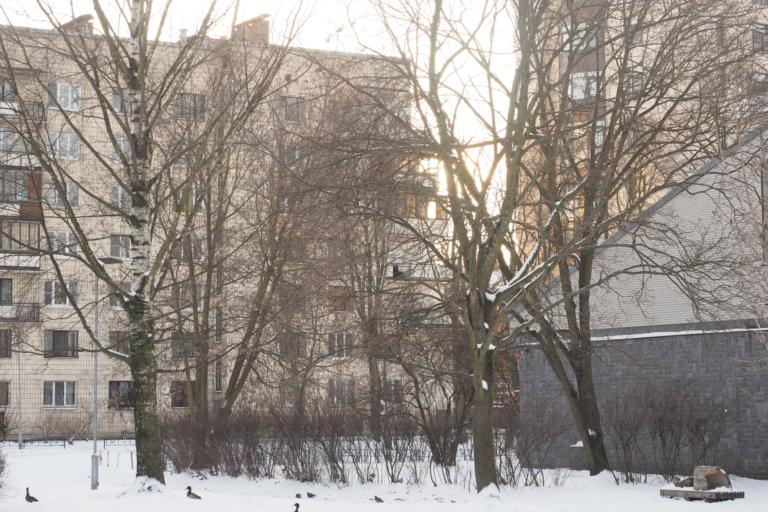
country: RU
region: Leningrad
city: Chernaya Rechka
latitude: 59.9736
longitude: 30.2976
